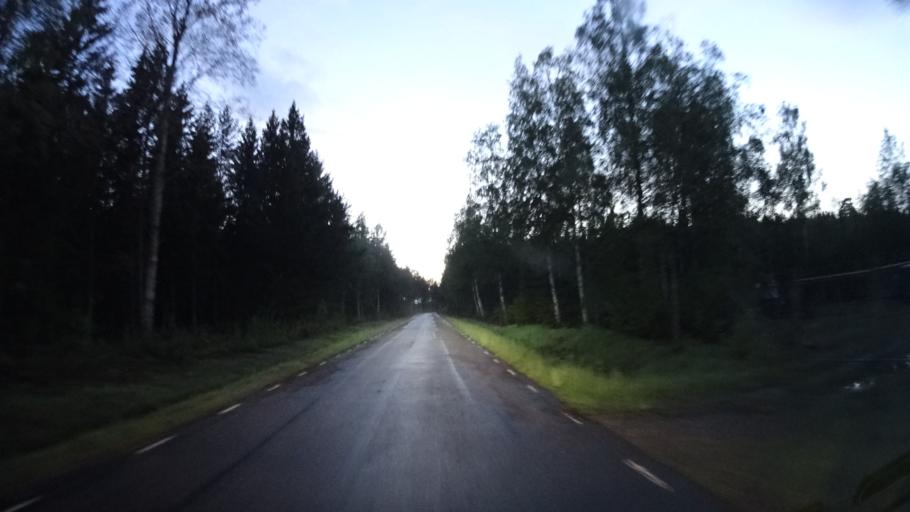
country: SE
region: Kalmar
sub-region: Vasterviks Kommun
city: Vaestervik
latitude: 57.7747
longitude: 16.5348
